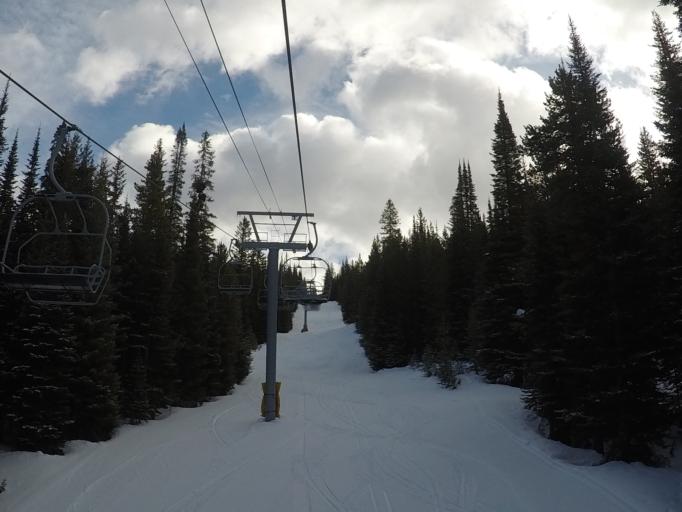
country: US
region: Montana
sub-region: Granite County
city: Philipsburg
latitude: 46.2516
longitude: -113.2277
